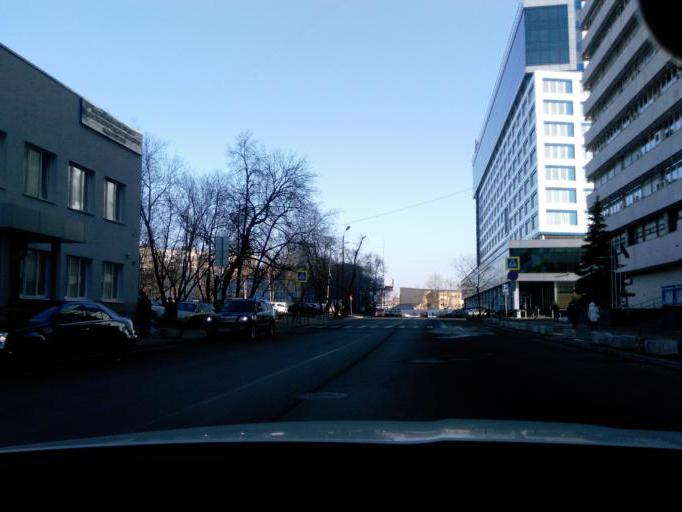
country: RU
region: Moscow
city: Mar'ina Roshcha
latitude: 55.7895
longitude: 37.5831
